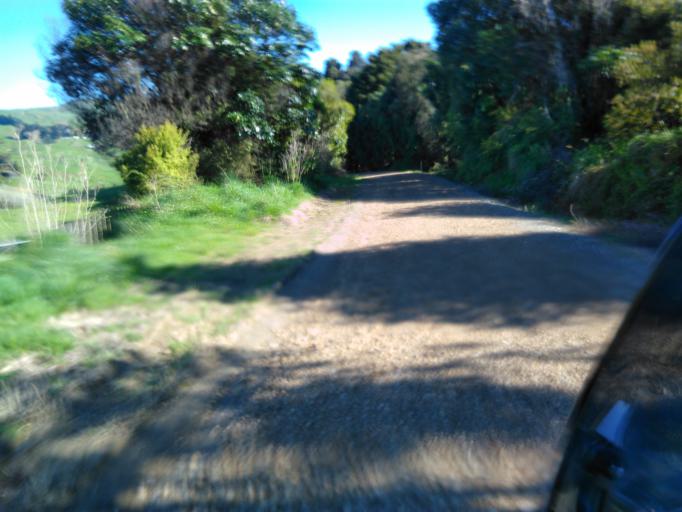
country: NZ
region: Gisborne
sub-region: Gisborne District
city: Gisborne
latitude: -38.3805
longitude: 177.6181
